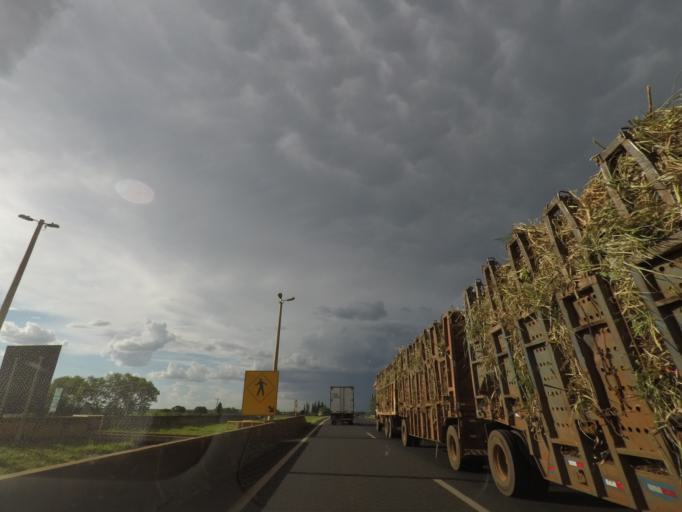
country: BR
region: Sao Paulo
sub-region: Jardinopolis
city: Jardinopolis
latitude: -21.0575
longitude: -47.8215
